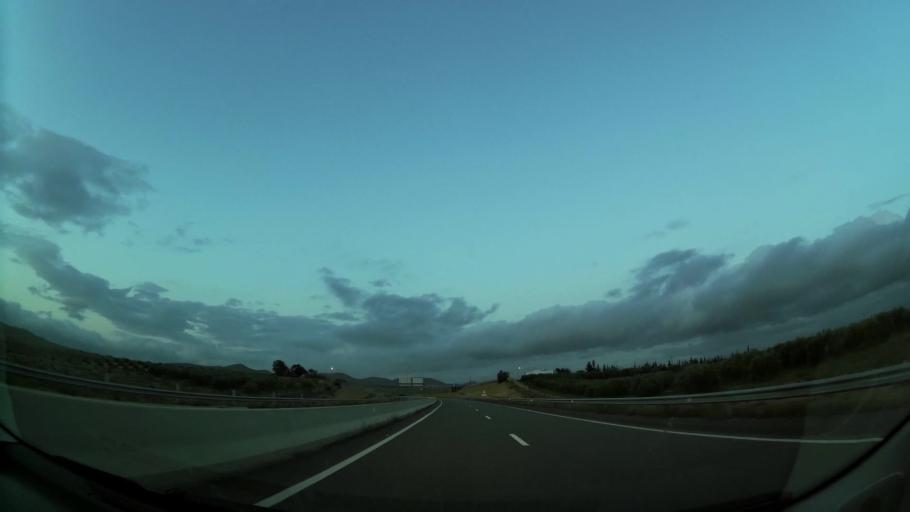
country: MA
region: Oriental
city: El Aioun
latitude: 34.6125
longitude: -2.4752
